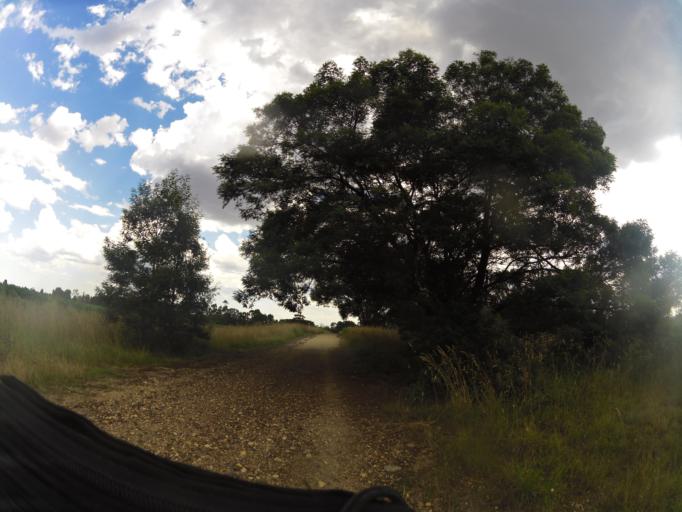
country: AU
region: Victoria
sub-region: Wellington
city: Heyfield
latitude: -38.0073
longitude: 146.6971
